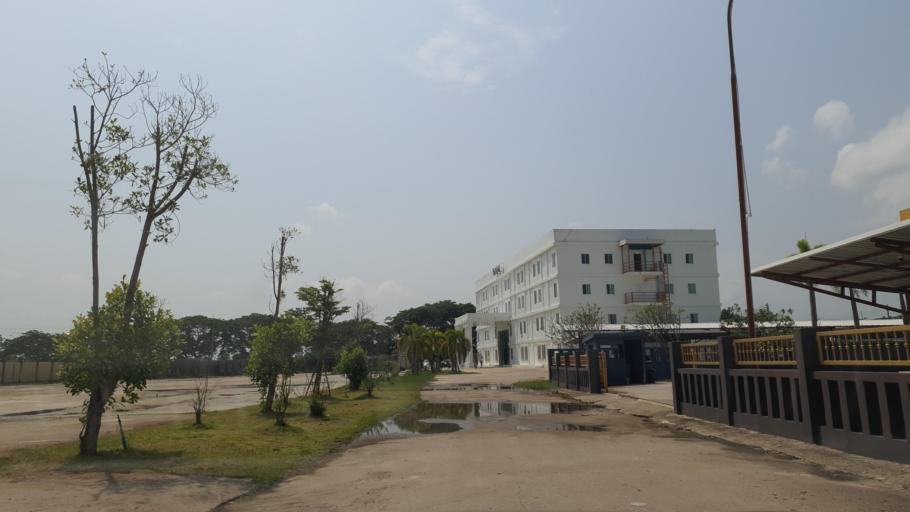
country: TH
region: Lamphun
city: Lamphun
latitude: 18.6040
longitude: 99.0126
